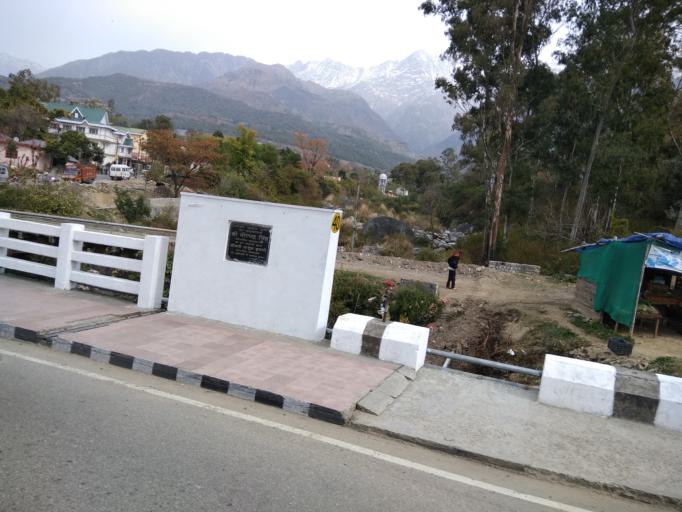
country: IN
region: Himachal Pradesh
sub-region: Kangra
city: Dharmsala
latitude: 32.1978
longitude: 76.3442
